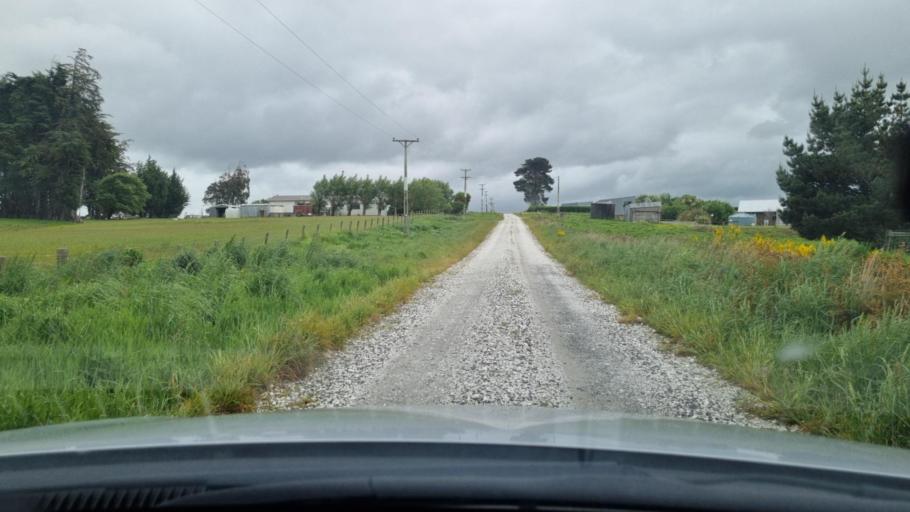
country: NZ
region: Southland
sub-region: Invercargill City
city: Invercargill
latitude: -46.4546
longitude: 168.3939
